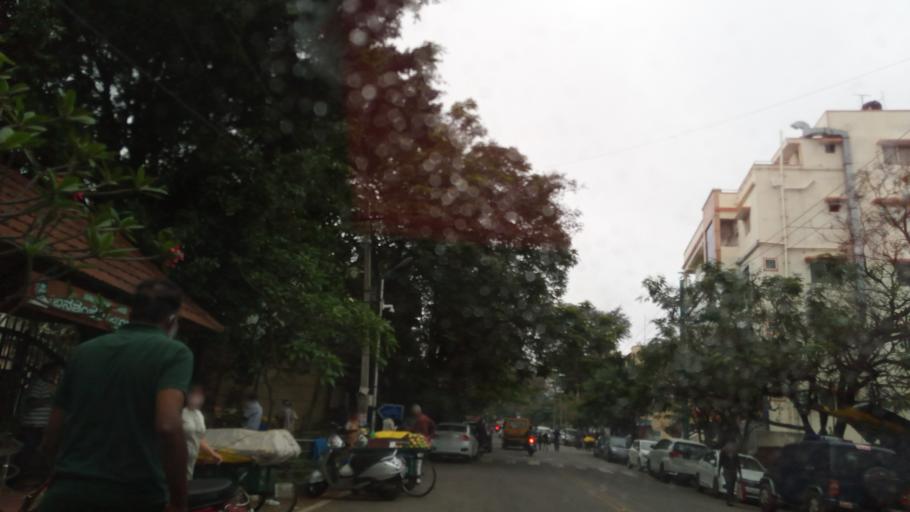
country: IN
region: Karnataka
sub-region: Bangalore Urban
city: Bangalore
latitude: 12.9241
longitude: 77.5665
